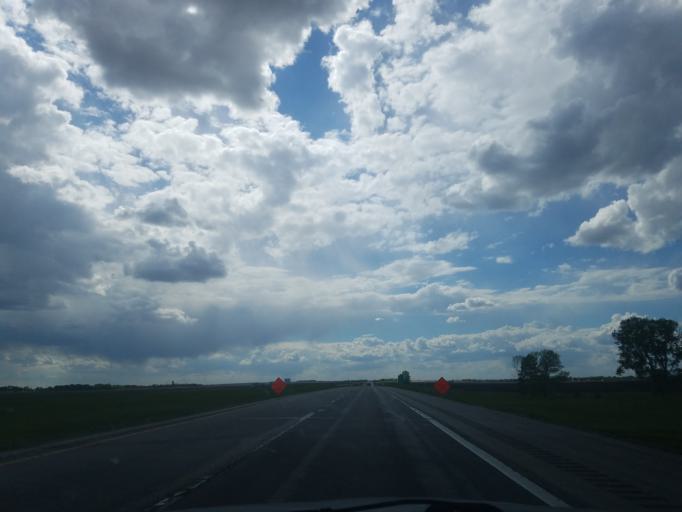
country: US
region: North Dakota
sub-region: Barnes County
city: Valley City
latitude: 46.9200
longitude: -97.7584
